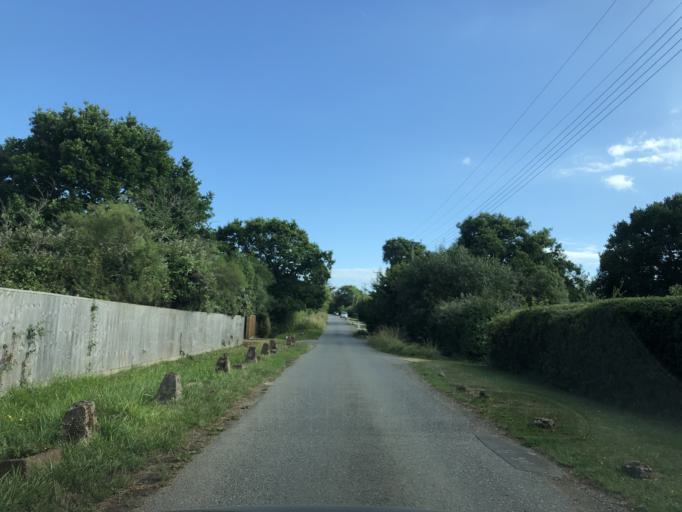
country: GB
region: England
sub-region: Isle of Wight
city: Shalfleet
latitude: 50.7065
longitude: -1.4495
